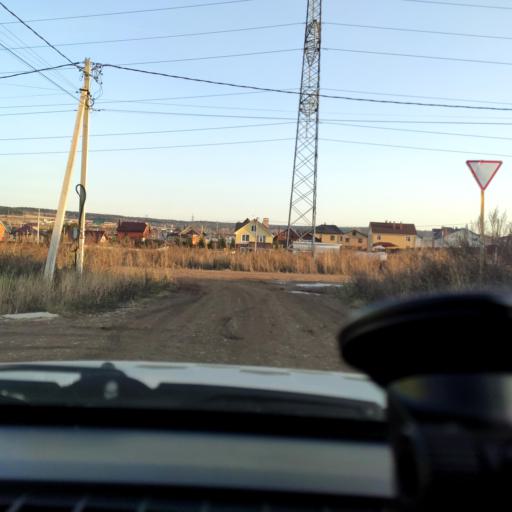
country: RU
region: Perm
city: Ferma
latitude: 57.9455
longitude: 56.3505
